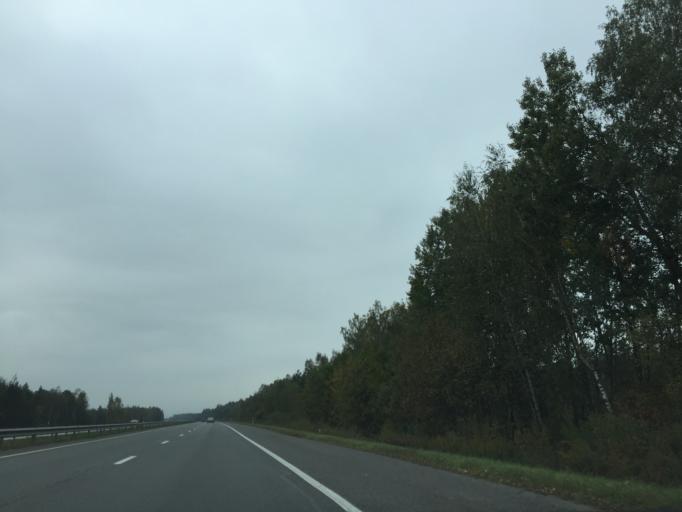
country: LV
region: Marupe
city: Marupe
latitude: 56.8746
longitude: 24.0688
